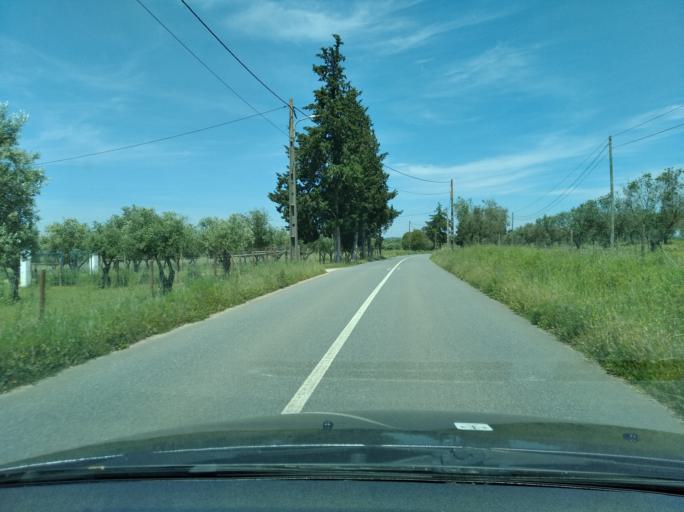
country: PT
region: Portalegre
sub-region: Avis
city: Avis
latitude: 39.0888
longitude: -7.8800
